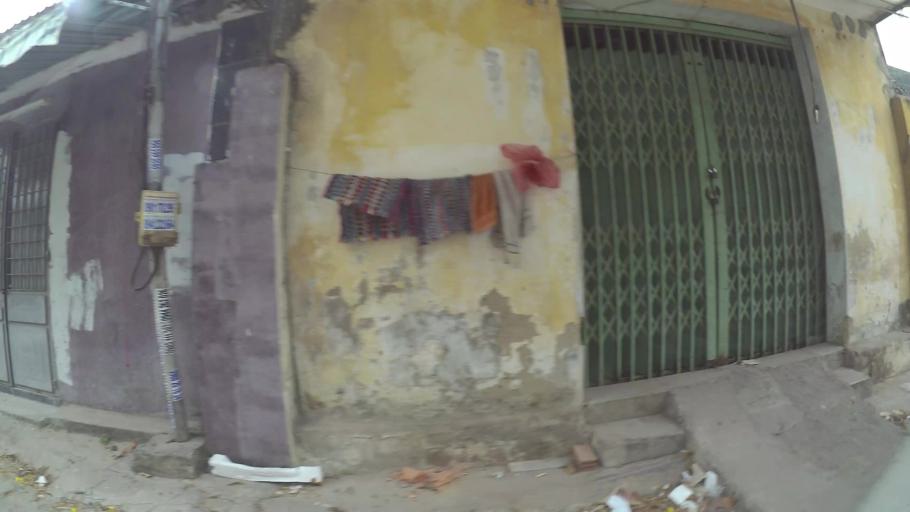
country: VN
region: Da Nang
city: Thanh Khe
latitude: 16.0675
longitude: 108.1976
